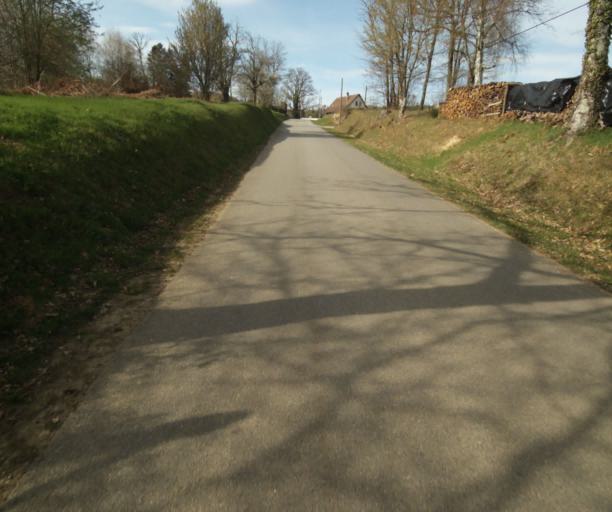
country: FR
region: Limousin
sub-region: Departement de la Correze
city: Naves
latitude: 45.3184
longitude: 1.7262
